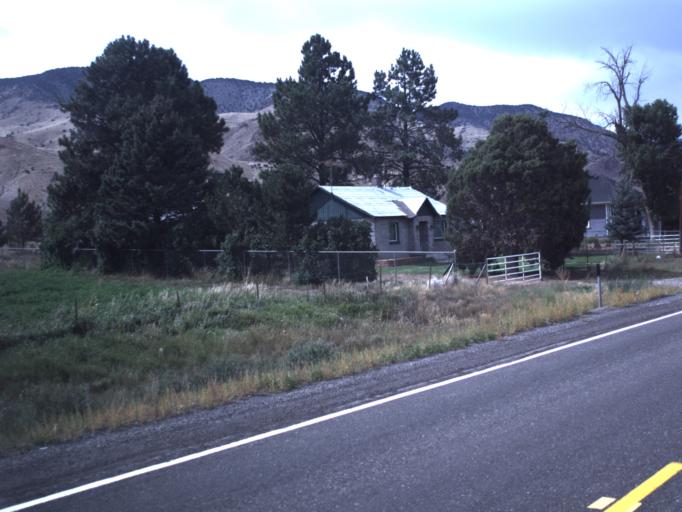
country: US
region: Utah
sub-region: Sevier County
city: Monroe
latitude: 38.4657
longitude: -112.2342
